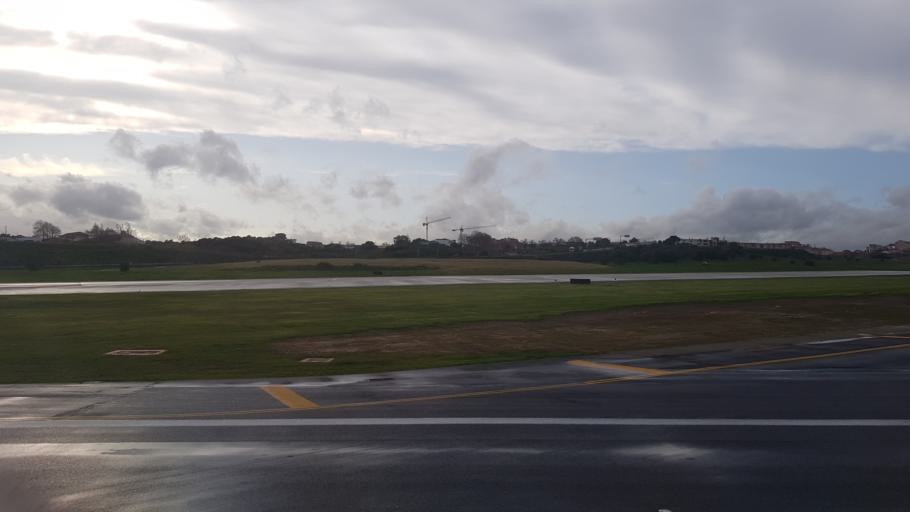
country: PT
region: Lisbon
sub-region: Loures
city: Camarate
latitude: 38.7836
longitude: -9.1348
